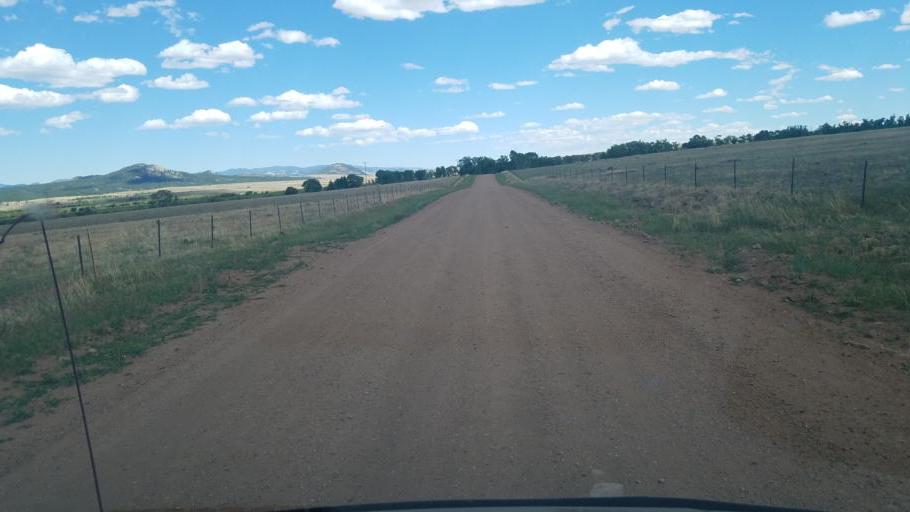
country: US
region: Colorado
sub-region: Custer County
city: Westcliffe
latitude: 38.2441
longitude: -105.6074
